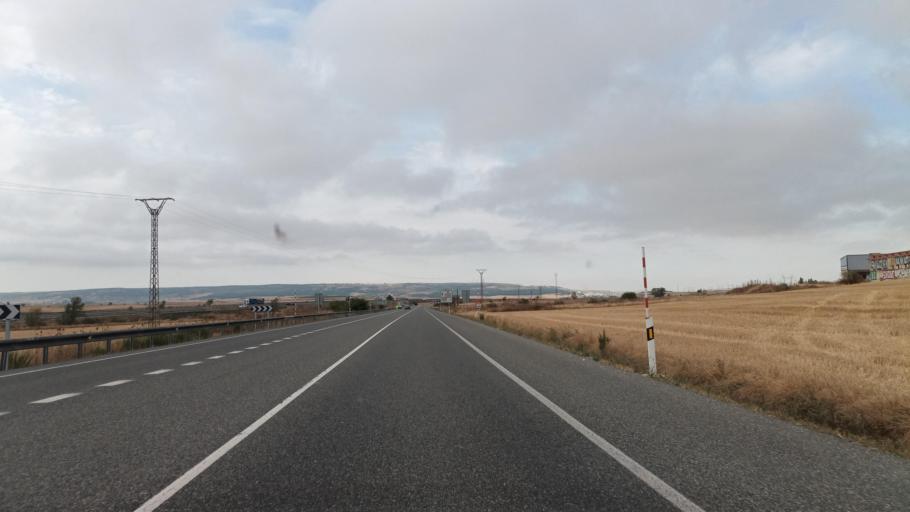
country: ES
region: Castille and Leon
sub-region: Provincia de Burgos
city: Fresno de Rodilla
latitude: 42.4301
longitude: -3.5035
